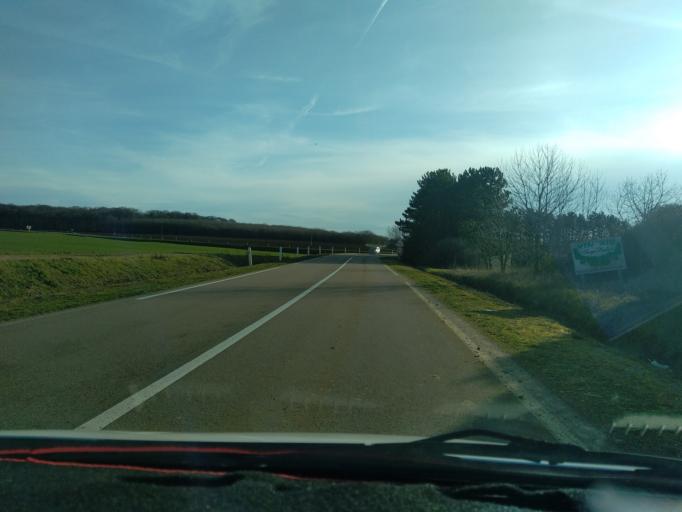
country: FR
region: Franche-Comte
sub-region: Departement de la Haute-Saone
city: Marnay
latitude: 47.3426
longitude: 5.6990
